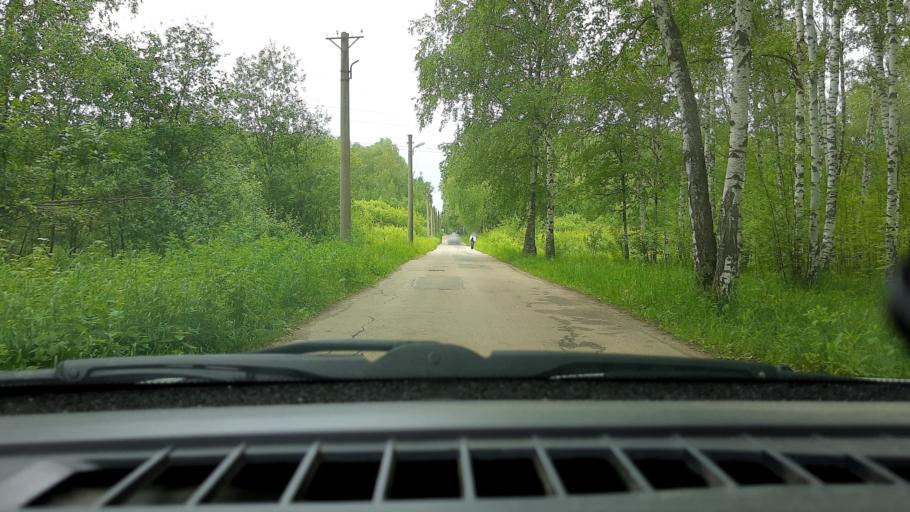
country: RU
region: Nizjnij Novgorod
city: Gorbatovka
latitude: 56.2869
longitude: 43.8300
